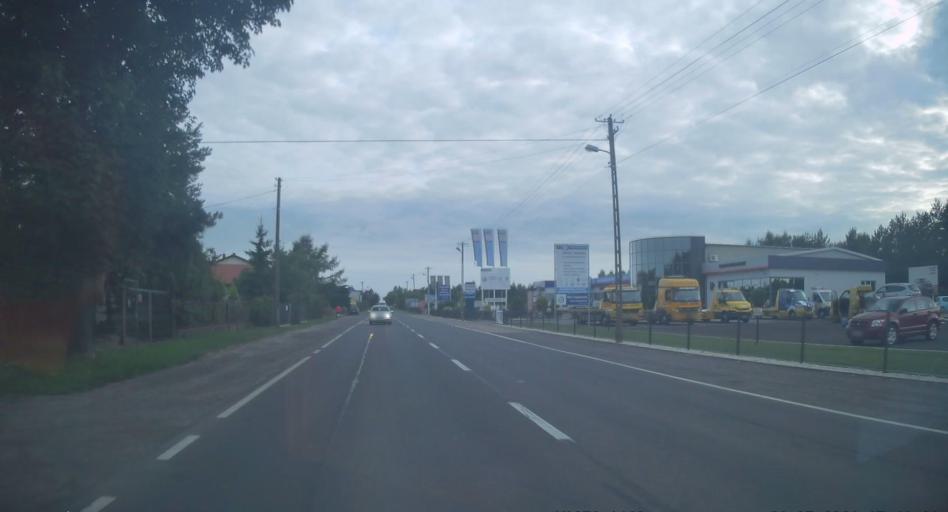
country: PL
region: Lodz Voivodeship
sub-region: Powiat radomszczanski
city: Radomsko
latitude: 51.1007
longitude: 19.4621
